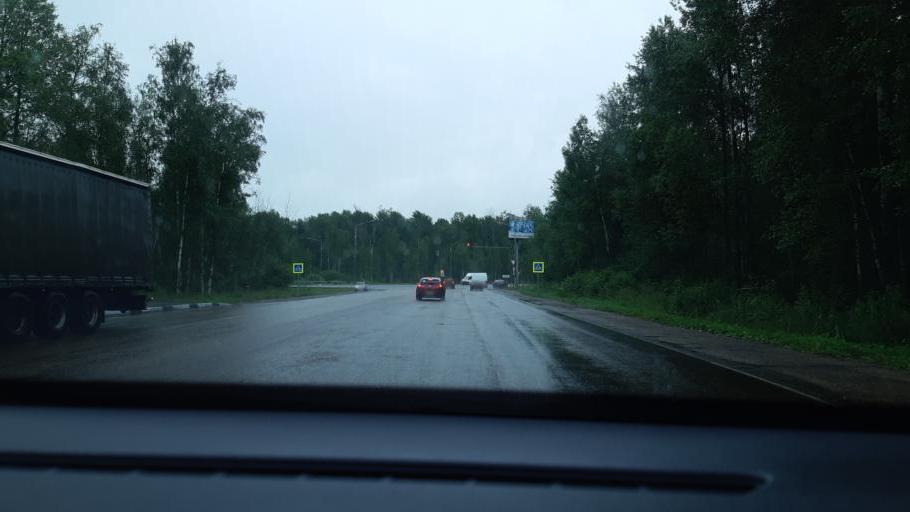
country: RU
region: Smolensk
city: Gagarin
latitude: 55.5010
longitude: 35.0363
